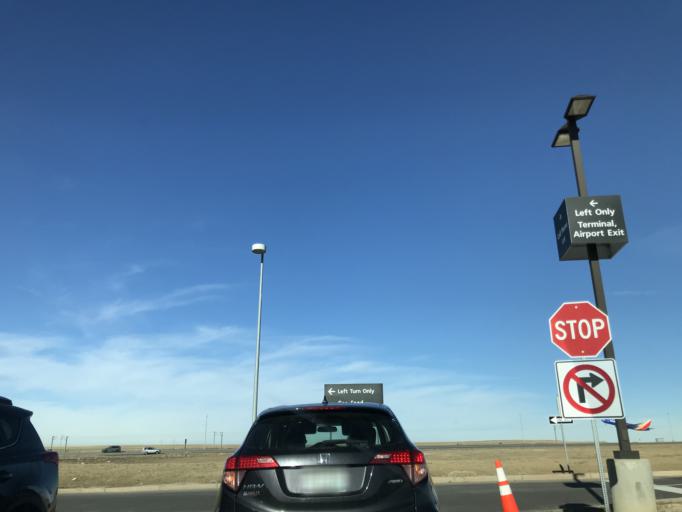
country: US
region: Colorado
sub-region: Adams County
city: Aurora
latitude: 39.8364
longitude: -104.7184
